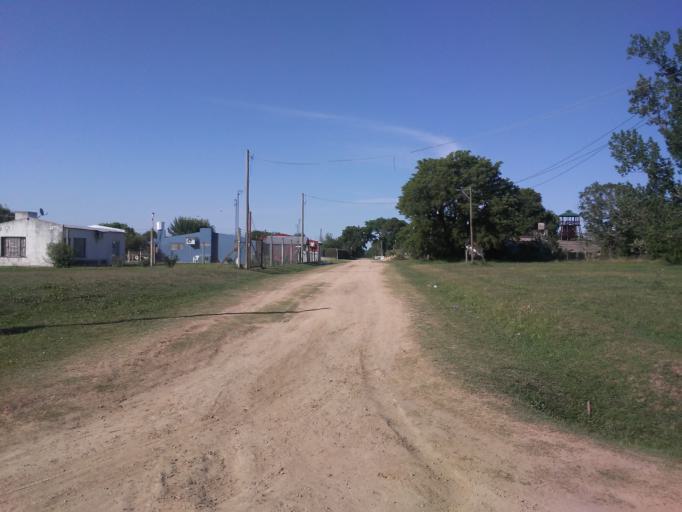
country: AR
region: Buenos Aires
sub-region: Partido de San Pedro
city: San Pedro
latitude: -33.5958
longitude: -59.8133
